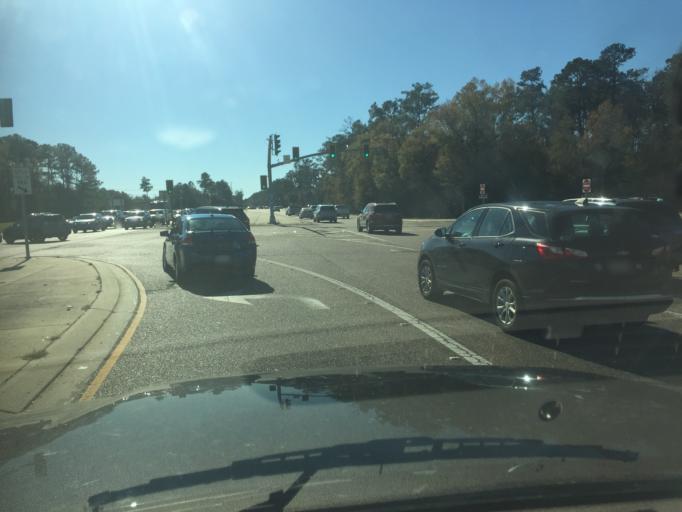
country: US
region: Louisiana
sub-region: Saint Tammany Parish
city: Covington
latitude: 30.4467
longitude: -90.1410
